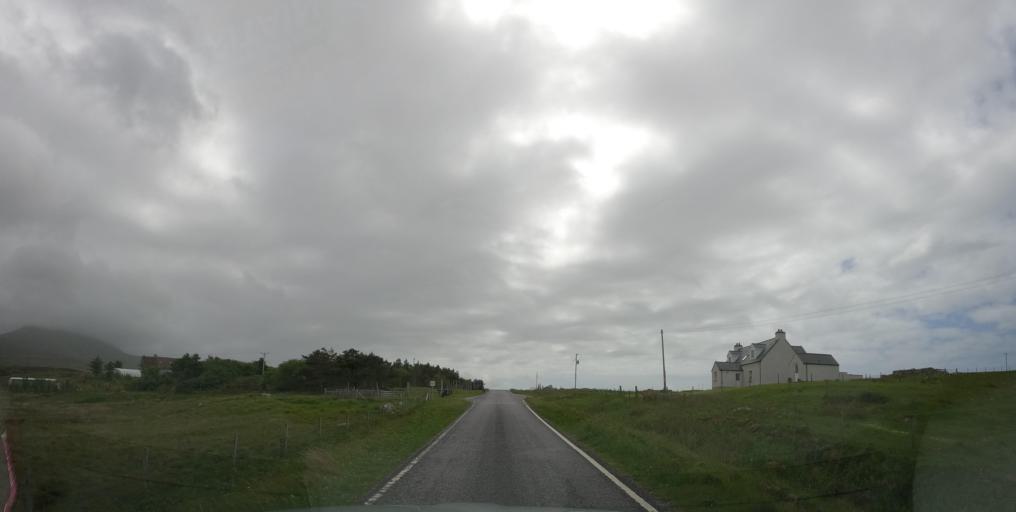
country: GB
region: Scotland
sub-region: Eilean Siar
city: Isle of South Uist
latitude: 57.2879
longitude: -7.3666
